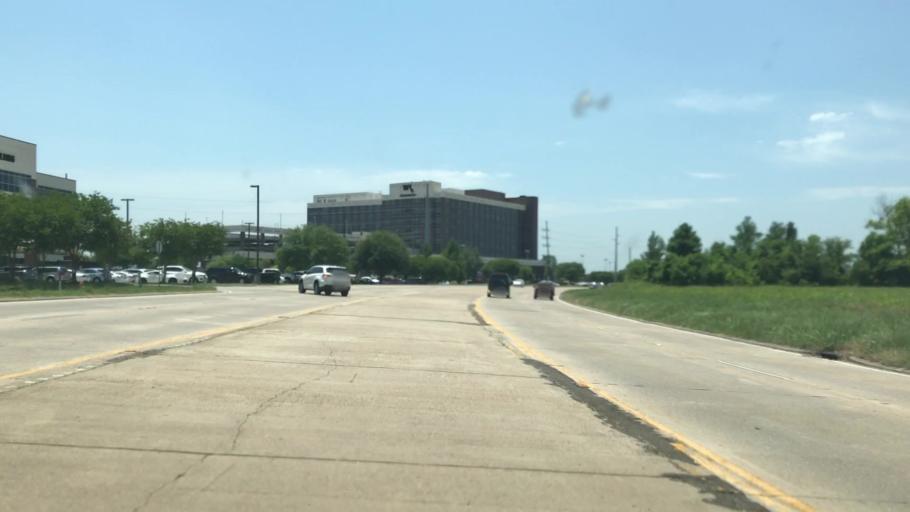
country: US
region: Louisiana
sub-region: Bossier Parish
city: Bossier City
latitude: 32.4351
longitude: -93.7076
